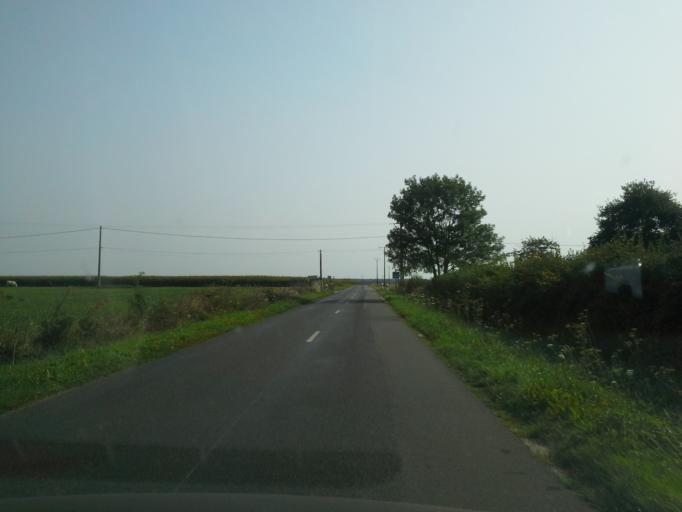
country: FR
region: Centre
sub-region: Departement du Loir-et-Cher
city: La Ville-aux-Clercs
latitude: 47.9092
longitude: 1.0636
